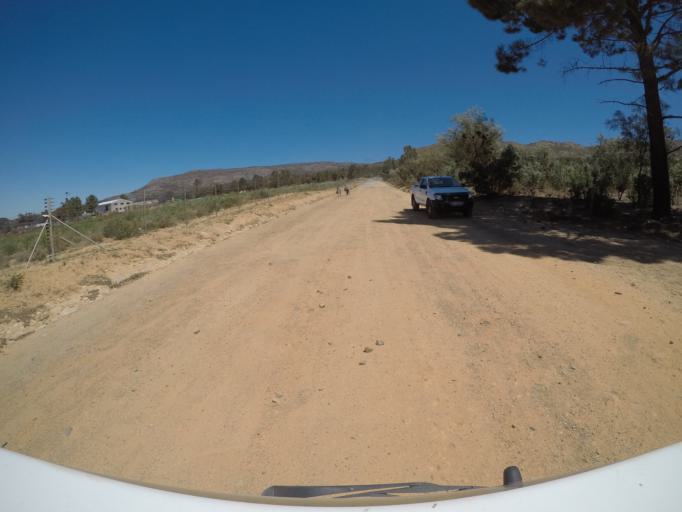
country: ZA
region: Western Cape
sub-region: Overberg District Municipality
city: Grabouw
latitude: -34.2228
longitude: 19.1908
